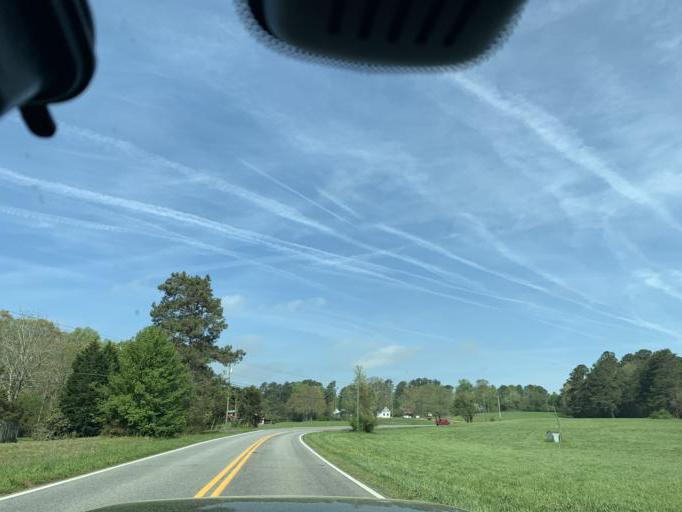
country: US
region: Georgia
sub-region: Forsyth County
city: Cumming
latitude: 34.2177
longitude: -84.0823
